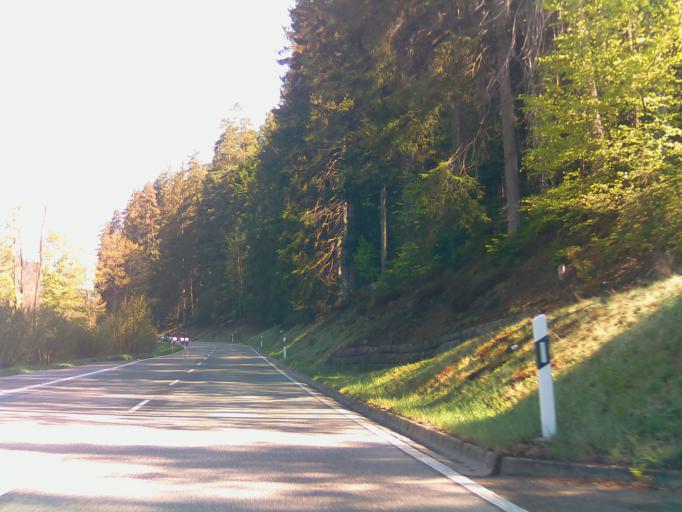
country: DE
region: Baden-Wuerttemberg
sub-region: Karlsruhe Region
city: Neuweiler
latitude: 48.6738
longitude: 8.5622
